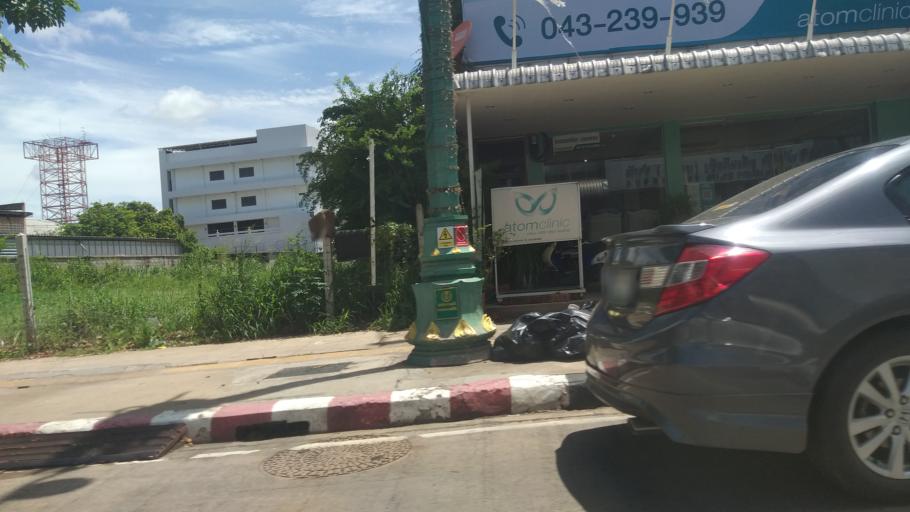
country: TH
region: Khon Kaen
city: Khon Kaen
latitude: 16.4312
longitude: 102.8297
